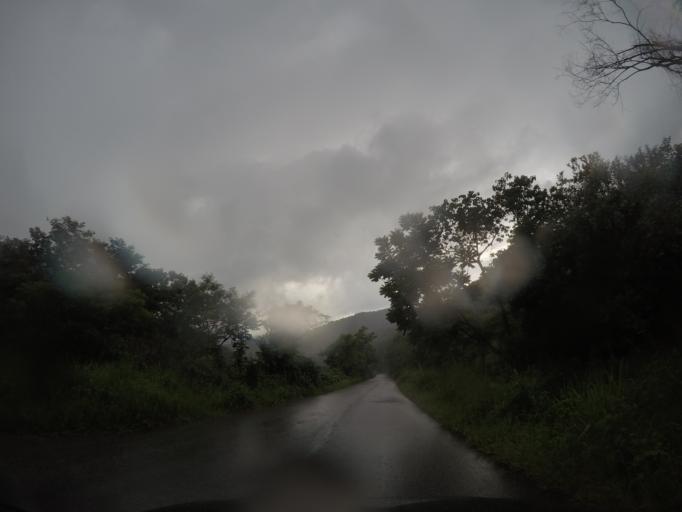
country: MX
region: Oaxaca
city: San Gabriel Mixtepec
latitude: 16.1137
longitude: -97.0655
